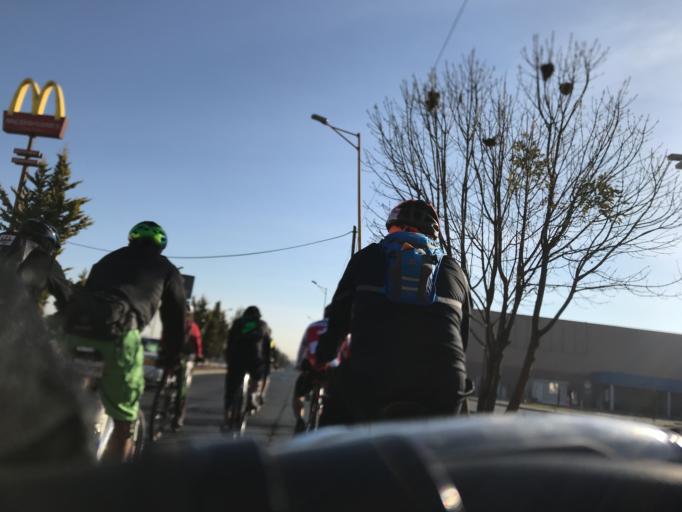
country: MX
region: Mexico
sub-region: Cuautitlan
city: La Trinidad
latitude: 19.6777
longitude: -99.1497
